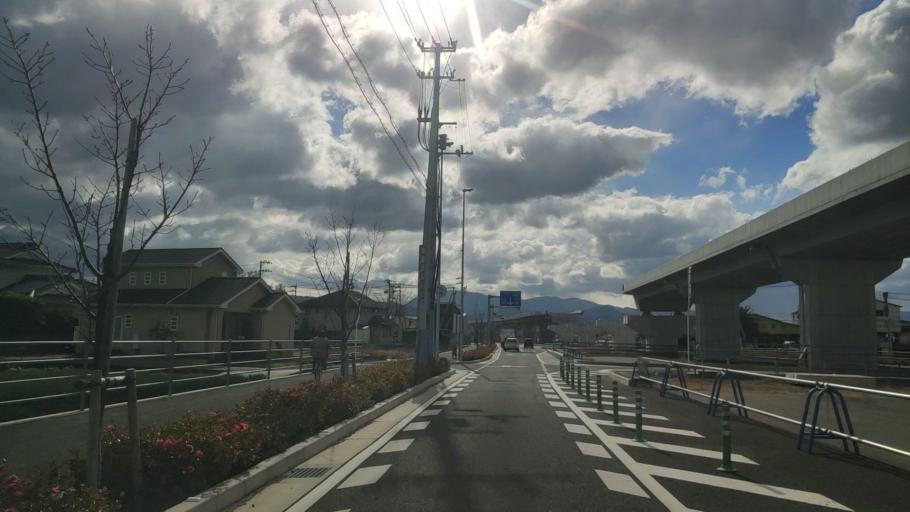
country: JP
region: Ehime
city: Masaki-cho
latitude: 33.8168
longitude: 132.7199
